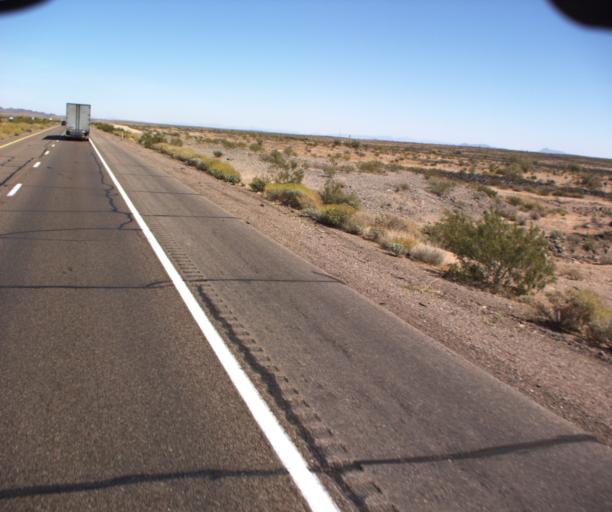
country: US
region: Arizona
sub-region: Maricopa County
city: Gila Bend
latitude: 32.8716
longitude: -113.1351
